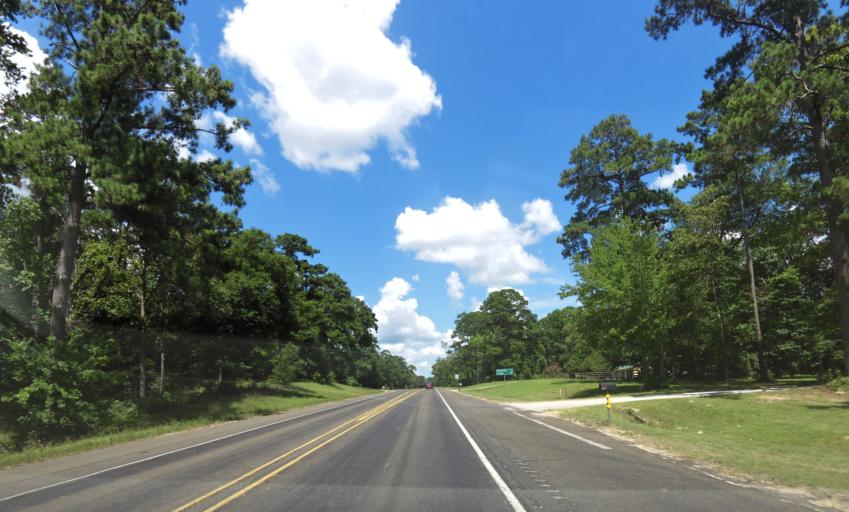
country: US
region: Texas
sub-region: Polk County
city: Livingston
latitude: 30.7176
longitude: -94.7110
